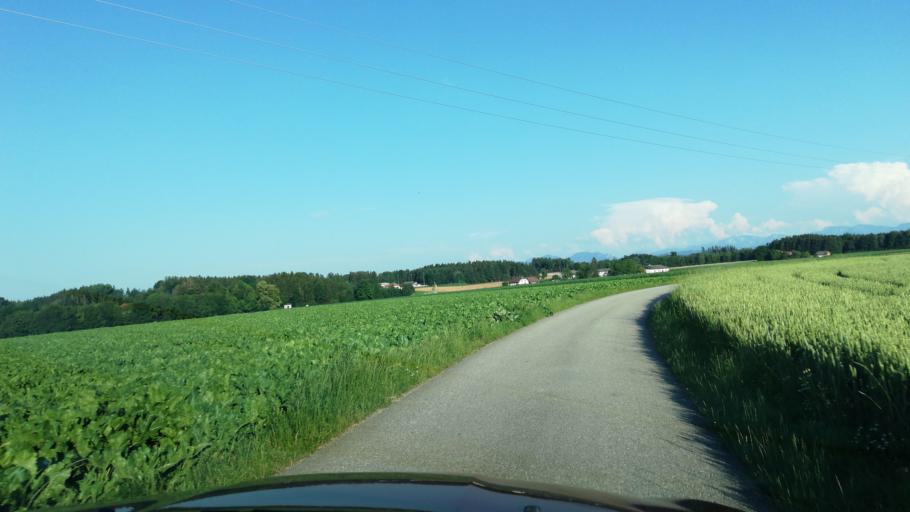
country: AT
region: Upper Austria
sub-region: Wels-Land
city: Sattledt
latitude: 48.0772
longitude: 14.0336
